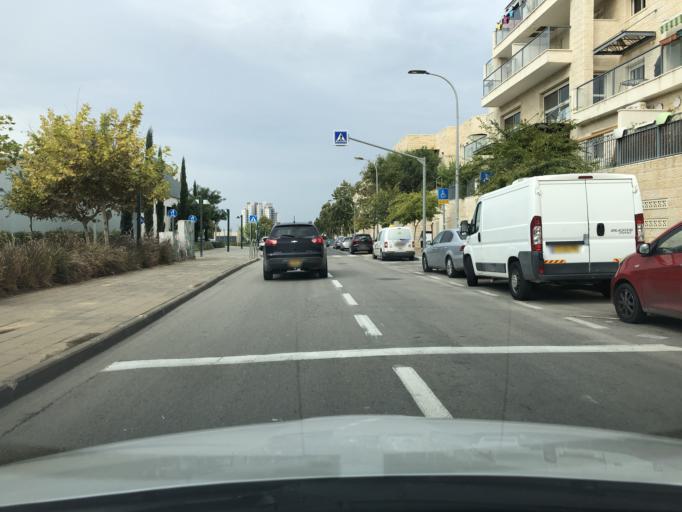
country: IL
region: Central District
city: Modiin
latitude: 31.9122
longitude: 35.0122
